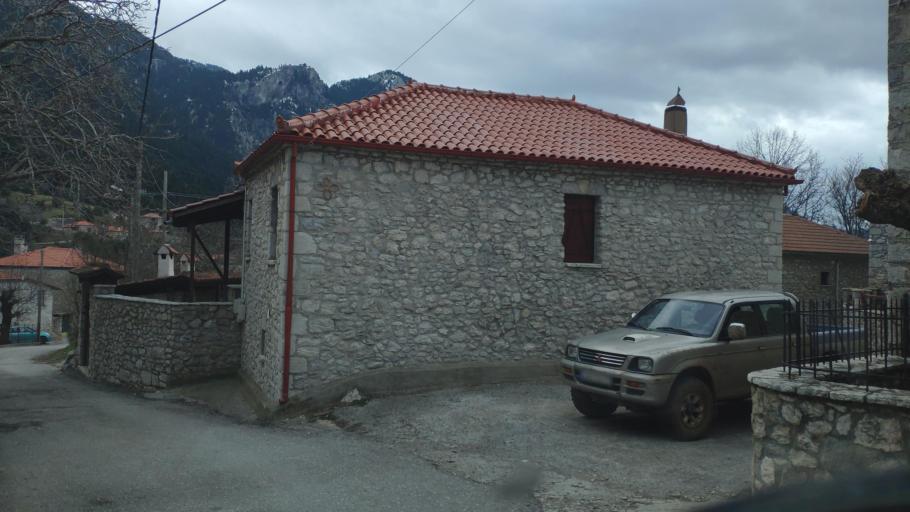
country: GR
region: Central Greece
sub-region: Nomos Fokidos
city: Amfissa
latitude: 38.6425
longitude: 22.4237
